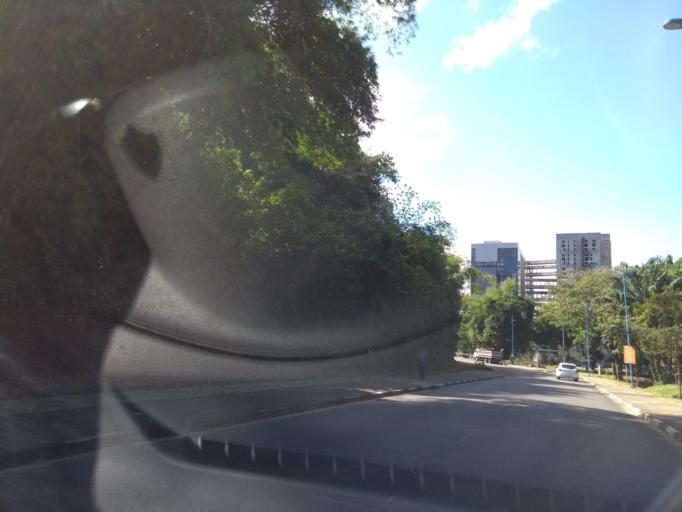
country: BR
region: Bahia
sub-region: Salvador
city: Salvador
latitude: -13.0048
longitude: -38.5111
